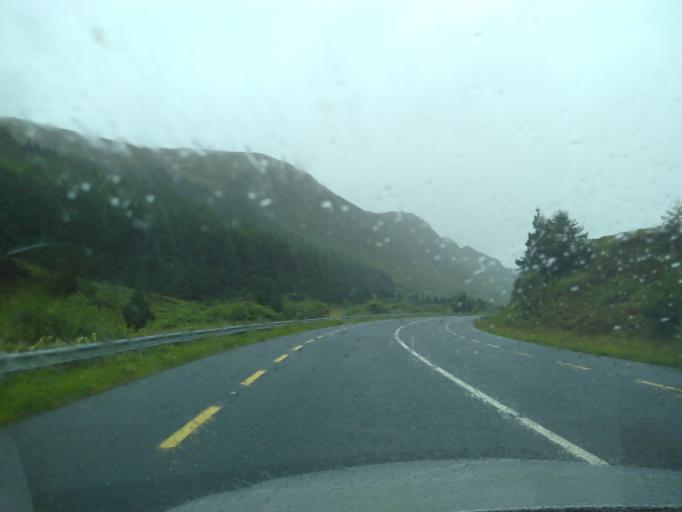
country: IE
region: Ulster
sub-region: County Donegal
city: Ballybofey
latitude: 54.7290
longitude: -7.9412
